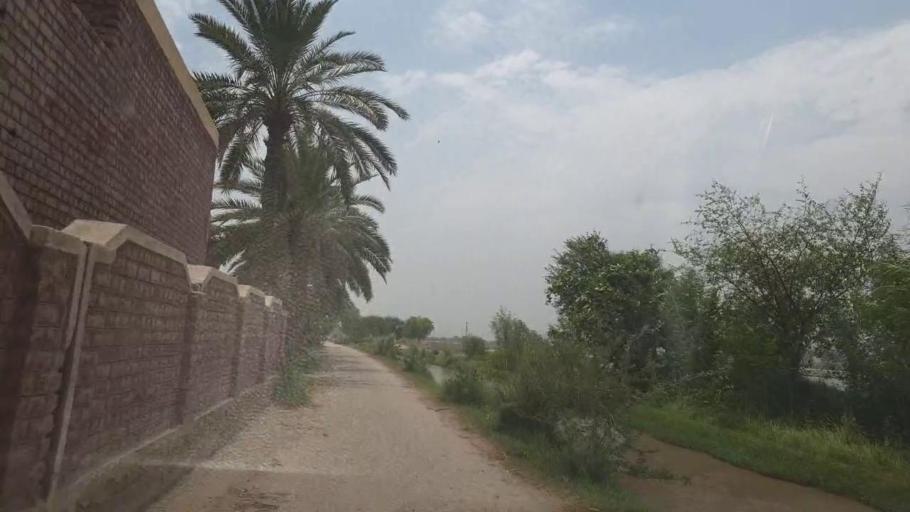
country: PK
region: Sindh
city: Kot Diji
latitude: 27.4428
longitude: 68.6752
